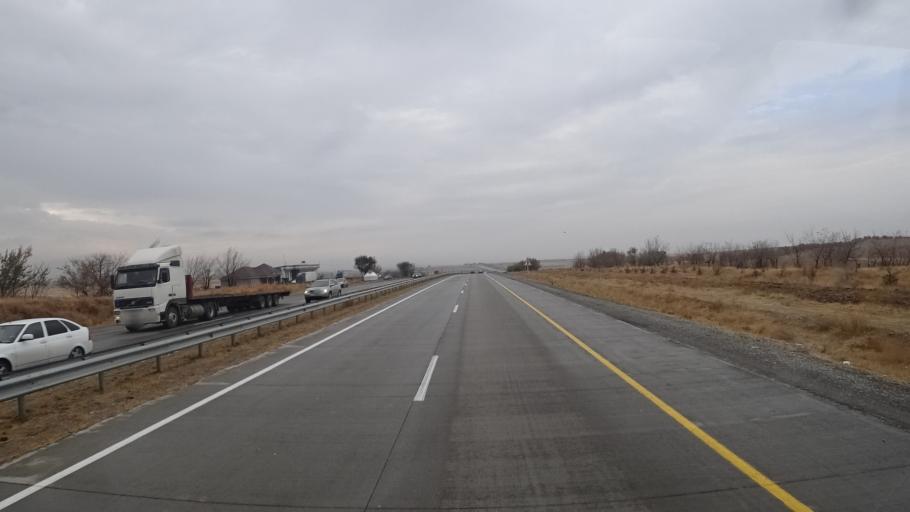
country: KZ
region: Ongtustik Qazaqstan
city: Sastobe
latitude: 42.4880
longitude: 69.9384
